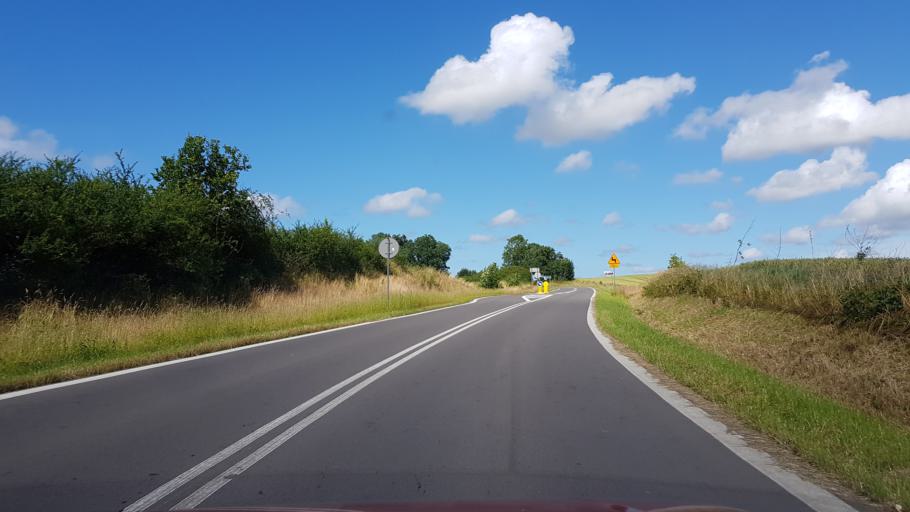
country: PL
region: West Pomeranian Voivodeship
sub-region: Powiat kolobrzeski
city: Ustronie Morskie
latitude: 54.1948
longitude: 15.9055
